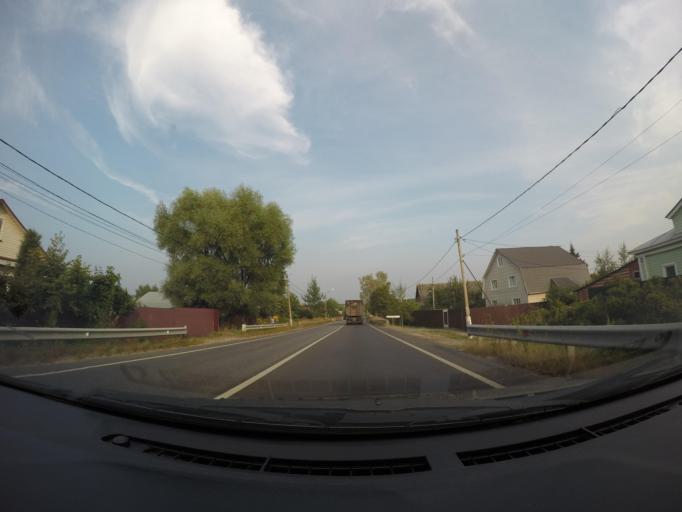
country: RU
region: Moskovskaya
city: Rechitsy
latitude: 55.5804
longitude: 38.5652
